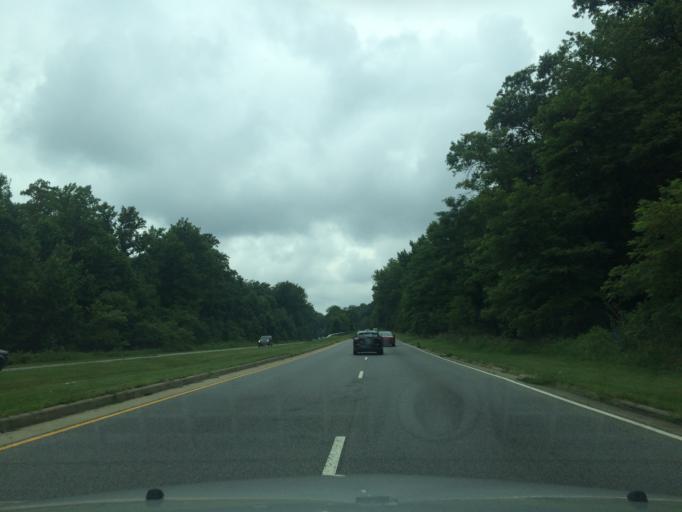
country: US
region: Maryland
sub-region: Prince George's County
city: Morningside
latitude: 38.8332
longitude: -76.8829
